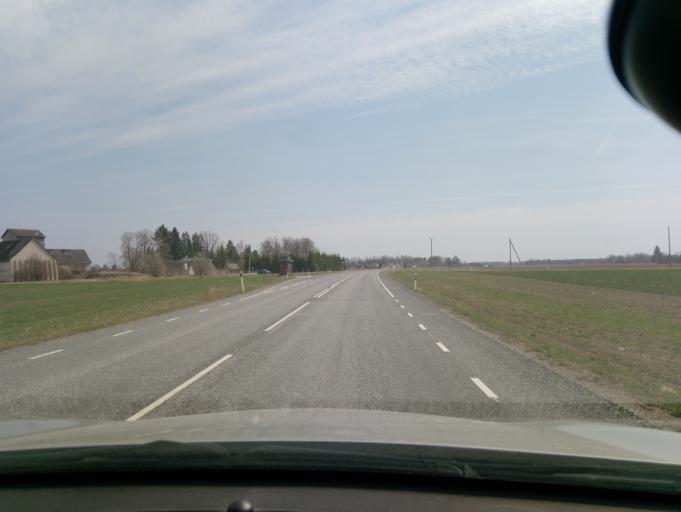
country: EE
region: Jaervamaa
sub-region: Tueri vald
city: Sarevere
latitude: 58.7623
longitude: 25.5478
